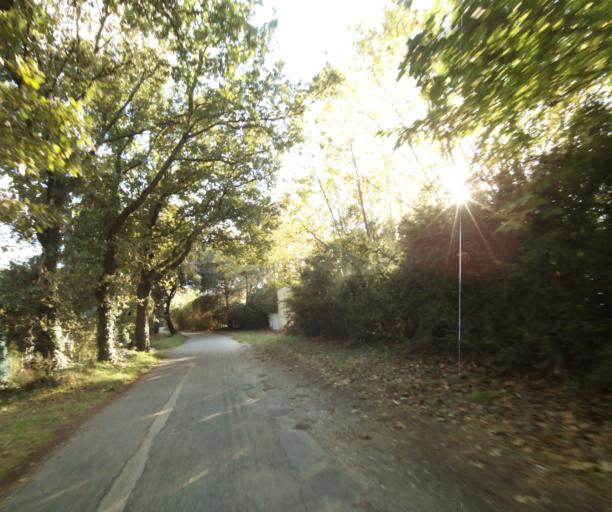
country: FR
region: Languedoc-Roussillon
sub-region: Departement des Pyrenees-Orientales
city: Argelers
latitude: 42.5663
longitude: 3.0135
